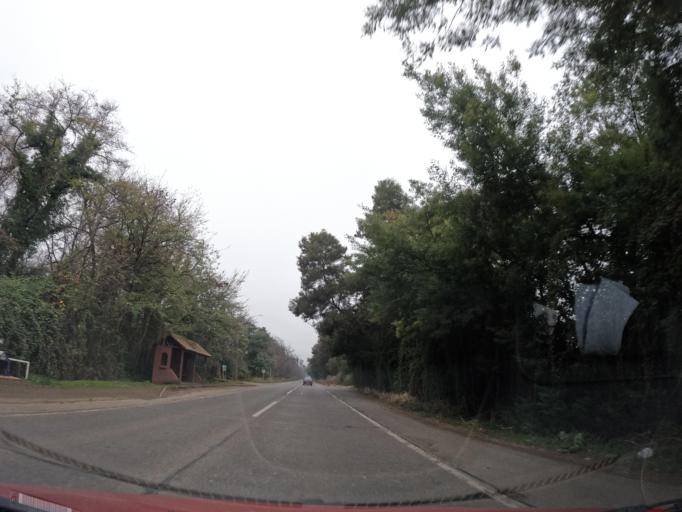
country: CL
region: Maule
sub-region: Provincia de Talca
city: San Clemente
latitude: -35.5619
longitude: -71.4570
